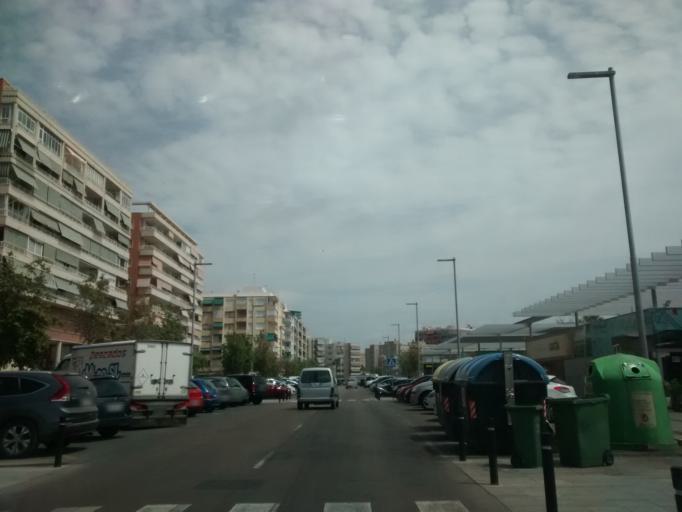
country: ES
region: Valencia
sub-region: Provincia de Alicante
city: Santa Pola
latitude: 38.1913
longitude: -0.5634
